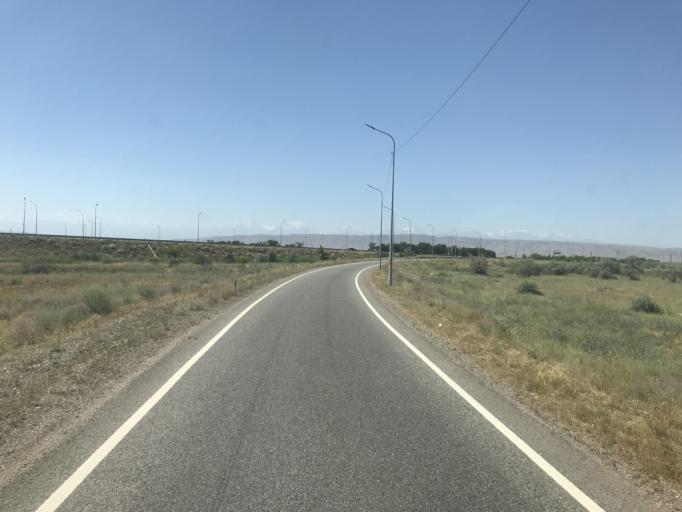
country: KZ
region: Zhambyl
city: Taraz
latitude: 42.8238
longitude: 71.1619
